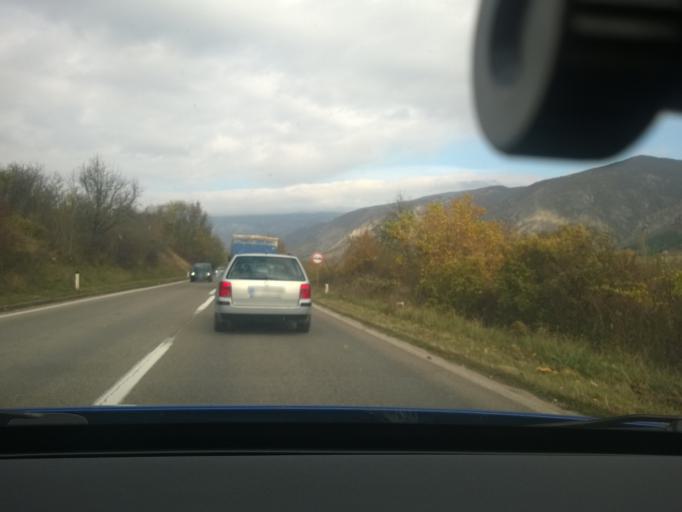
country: RS
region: Central Serbia
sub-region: Pirotski Okrug
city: Bela Palanka
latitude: 43.2832
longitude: 22.2213
